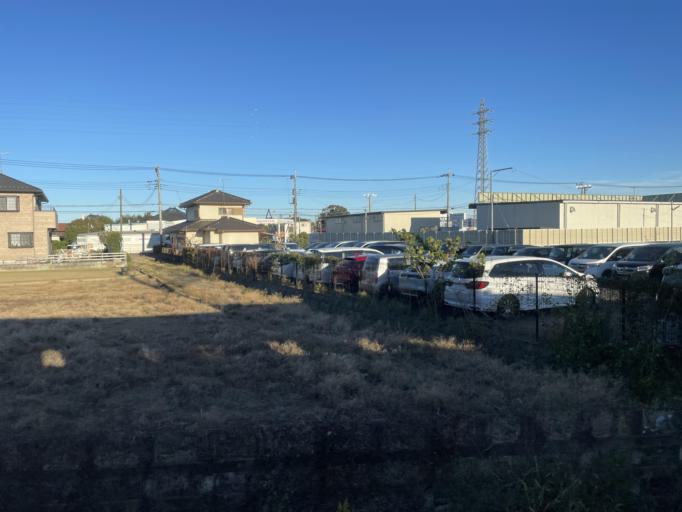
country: JP
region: Saitama
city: Satte
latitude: 36.0582
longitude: 139.7134
